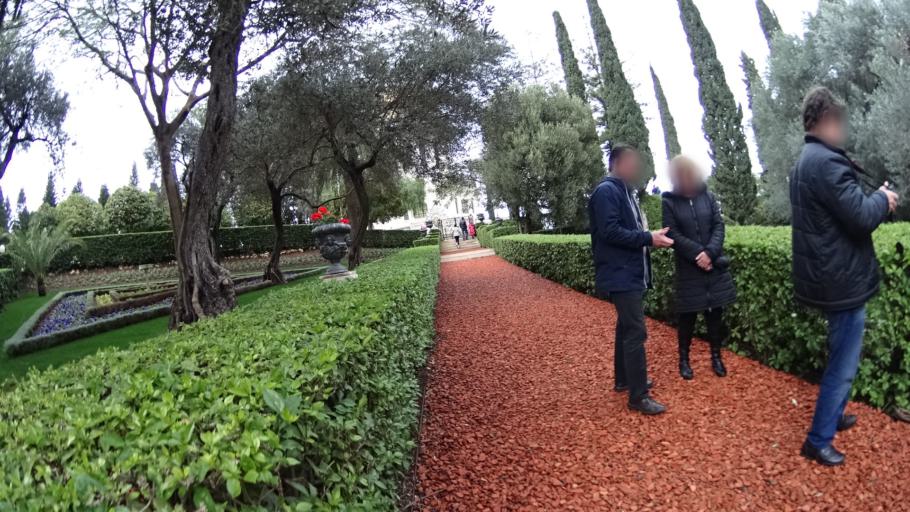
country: IL
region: Haifa
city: Haifa
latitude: 32.8140
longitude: 34.9874
